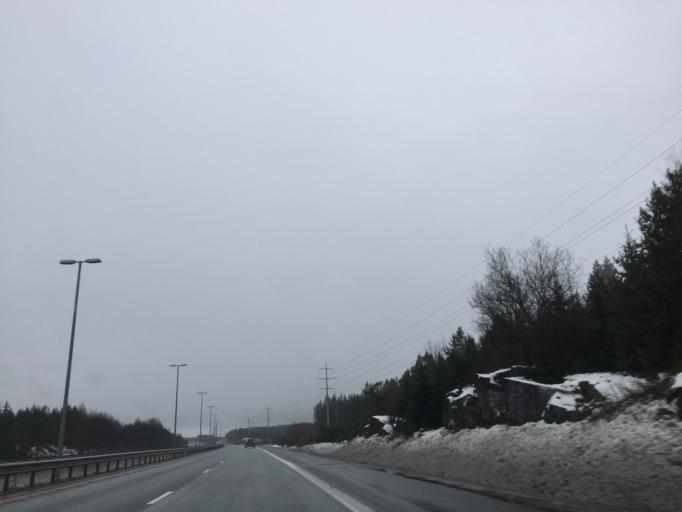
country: NO
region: Akershus
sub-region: Vestby
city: Vestby
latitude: 59.5638
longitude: 10.7208
